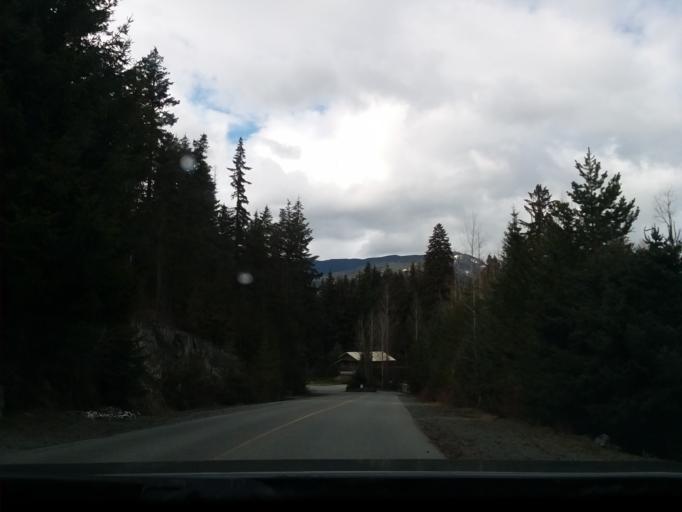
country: CA
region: British Columbia
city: Whistler
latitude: 50.1212
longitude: -122.9696
